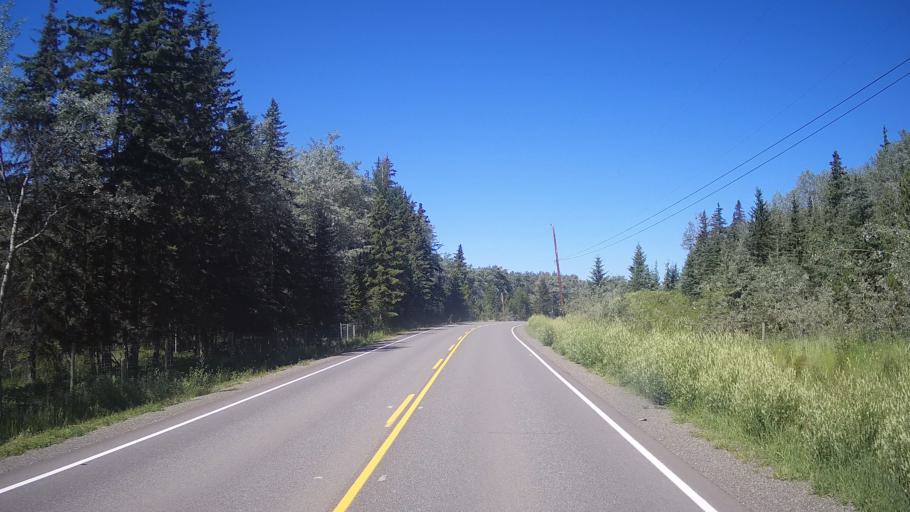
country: CA
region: British Columbia
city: Cache Creek
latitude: 51.5403
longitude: -121.0469
